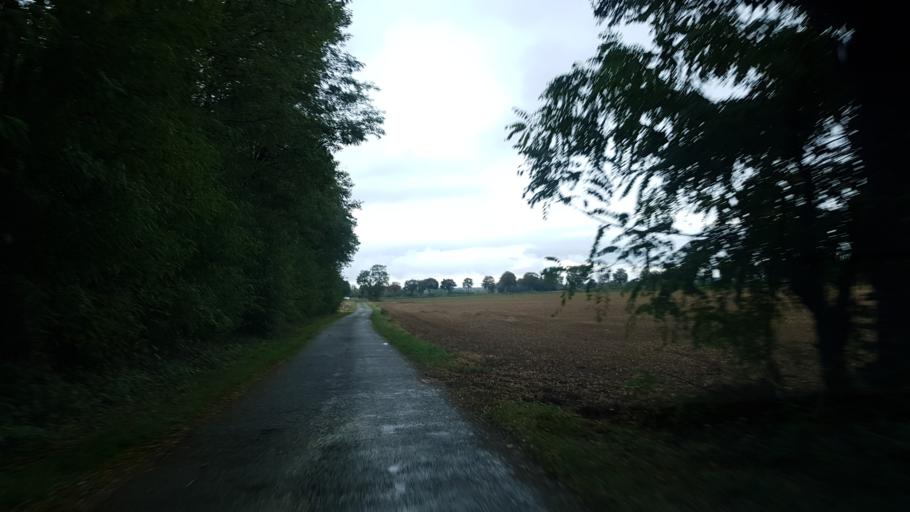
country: FR
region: Rhone-Alpes
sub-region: Departement de l'Ain
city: Tossiat
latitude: 46.1244
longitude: 5.2999
